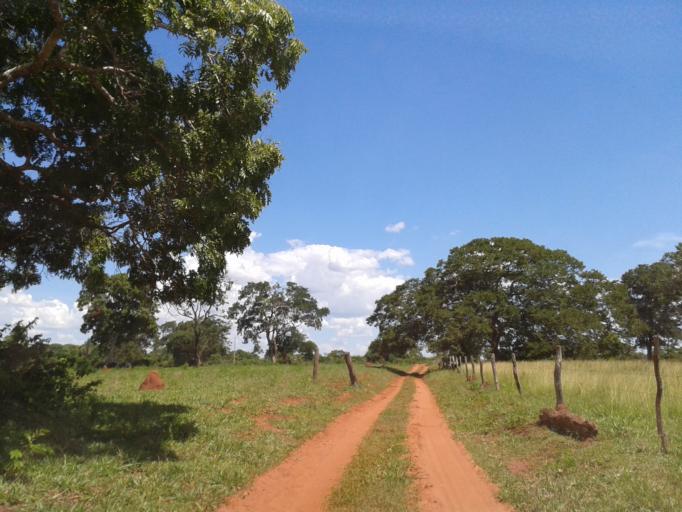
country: BR
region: Minas Gerais
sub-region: Santa Vitoria
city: Santa Vitoria
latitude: -19.1326
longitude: -50.5561
